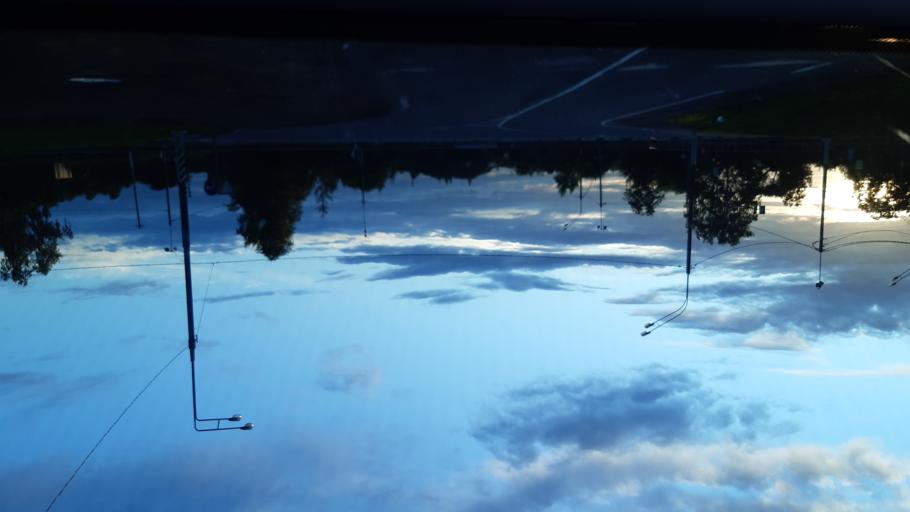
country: RU
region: Smolensk
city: Safonovo
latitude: 55.1320
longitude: 33.1977
